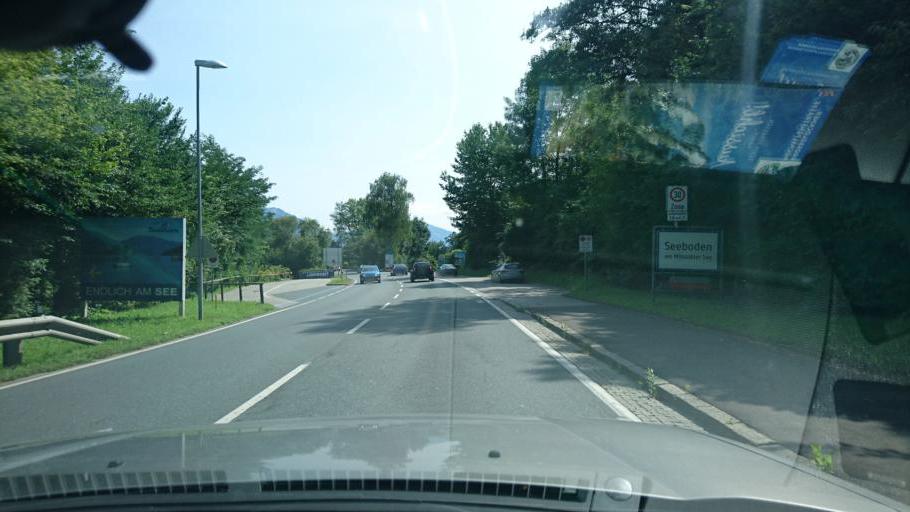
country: AT
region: Carinthia
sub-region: Politischer Bezirk Spittal an der Drau
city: Seeboden
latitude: 46.8155
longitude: 13.5028
